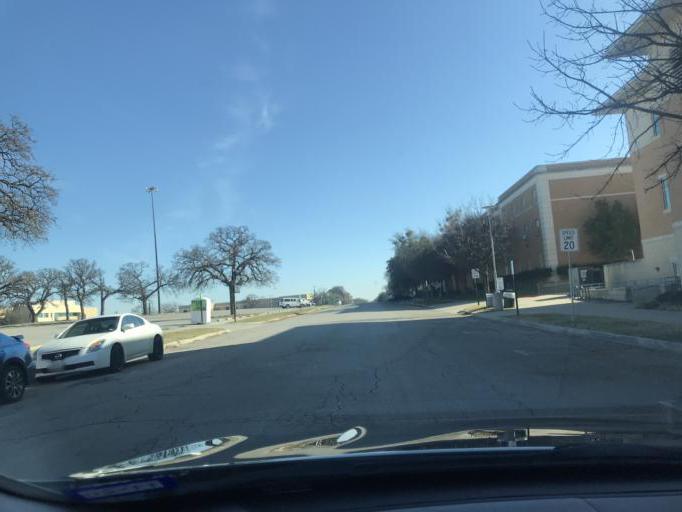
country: US
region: Texas
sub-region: Denton County
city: Denton
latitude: 33.2127
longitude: -97.1527
